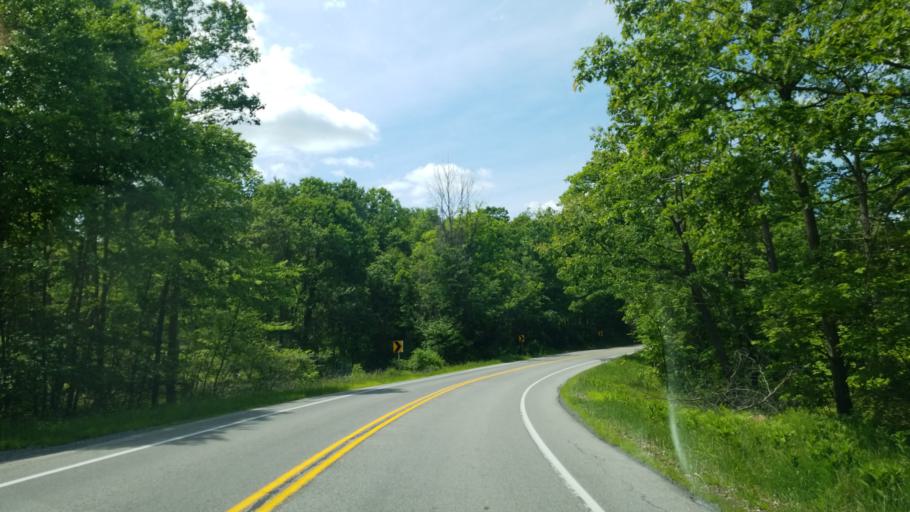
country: US
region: Pennsylvania
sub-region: Blair County
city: Tipton
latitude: 40.7018
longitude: -78.3055
